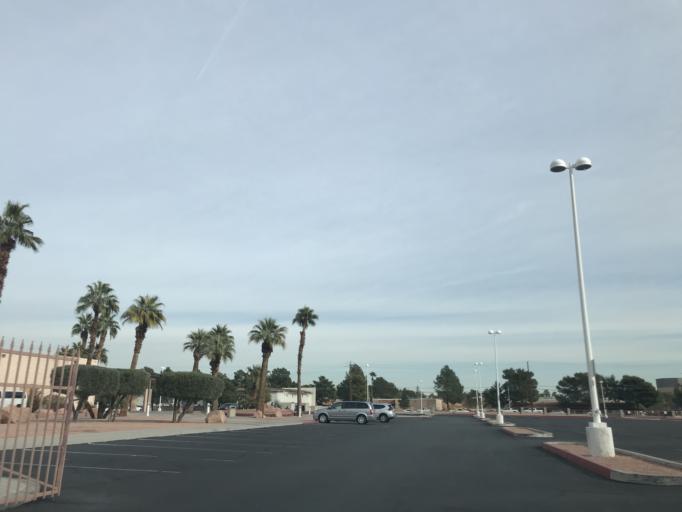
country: US
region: Nevada
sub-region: Clark County
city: Paradise
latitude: 36.0961
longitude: -115.1703
